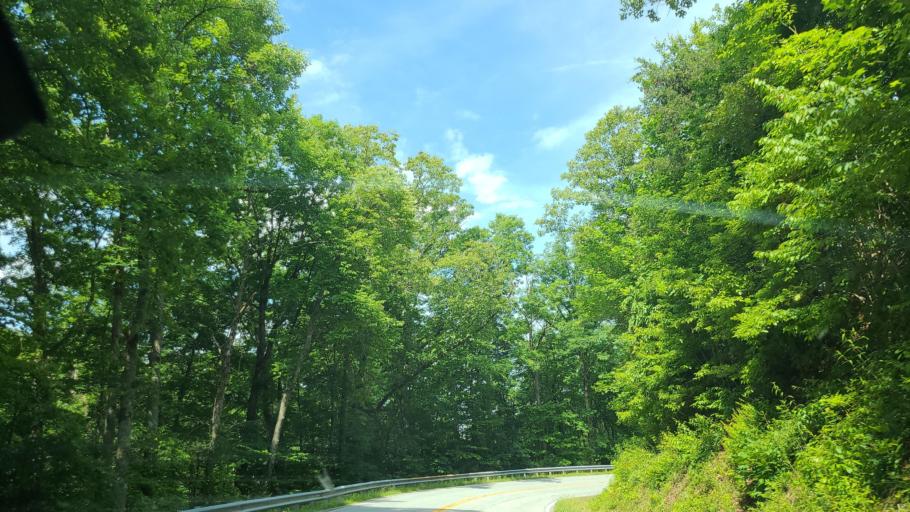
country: US
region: South Carolina
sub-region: Oconee County
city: Walhalla
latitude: 34.8967
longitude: -83.1729
